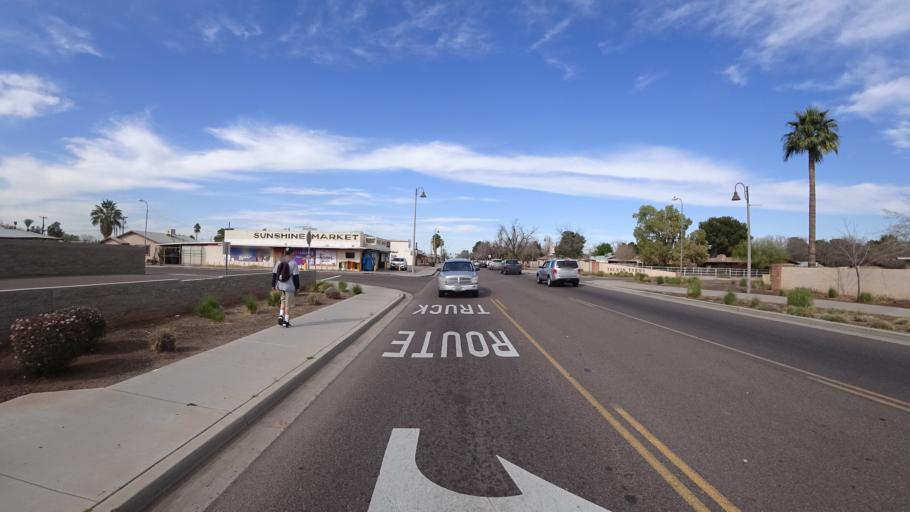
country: US
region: Arizona
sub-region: Maricopa County
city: Tolleson
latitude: 33.4512
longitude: -112.2551
